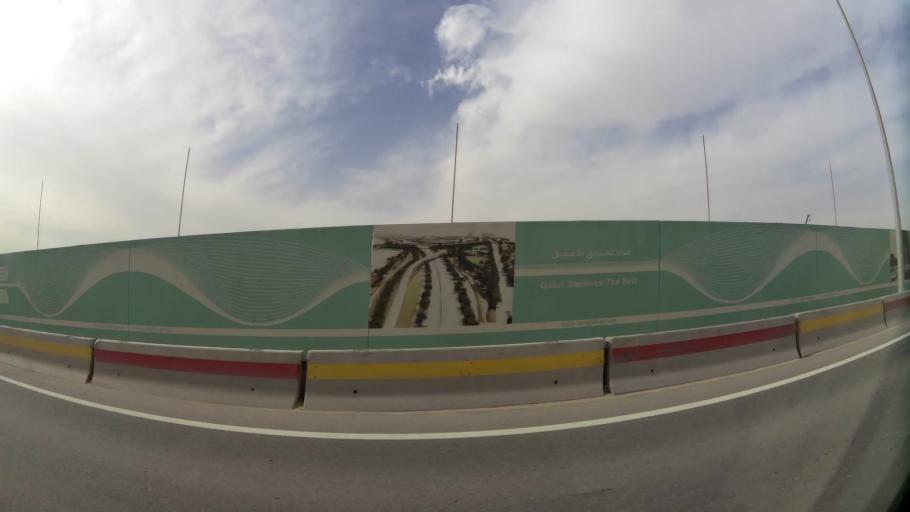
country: QA
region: Baladiyat ar Rayyan
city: Ar Rayyan
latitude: 25.3070
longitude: 51.4076
